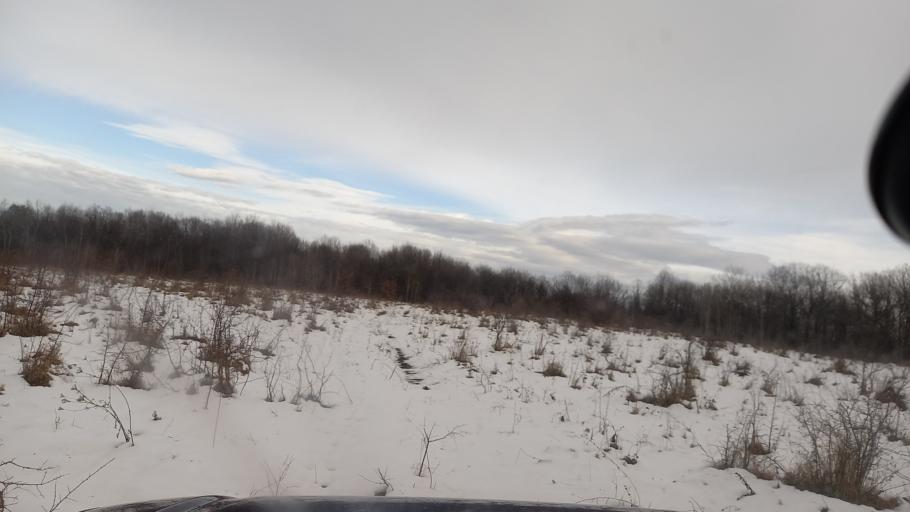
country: RU
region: Adygeya
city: Kamennomostskiy
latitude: 44.2530
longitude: 40.1805
